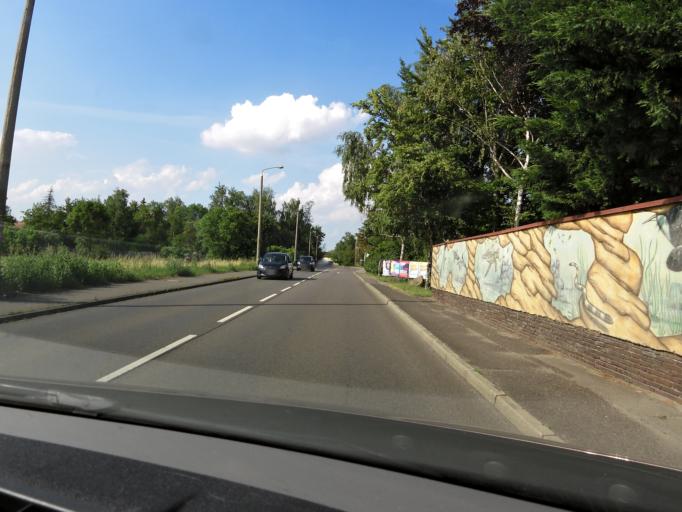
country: DE
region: Saxony
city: Taucha
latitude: 51.3380
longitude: 12.4440
